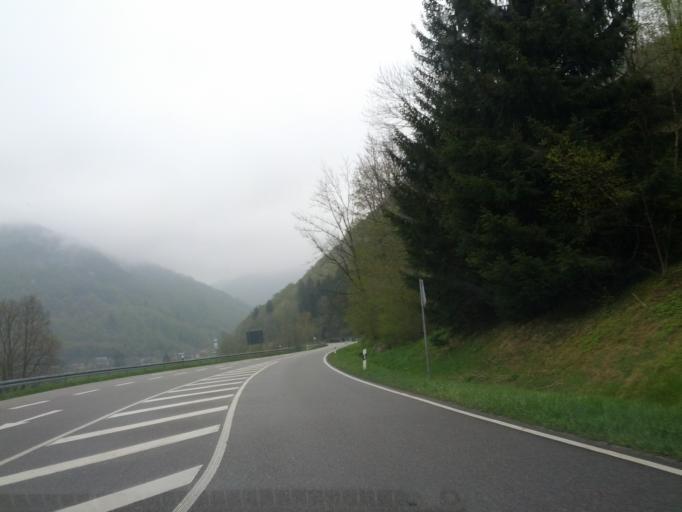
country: DE
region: Baden-Wuerttemberg
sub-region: Freiburg Region
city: Utzenfeld
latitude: 47.8019
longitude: 7.9257
